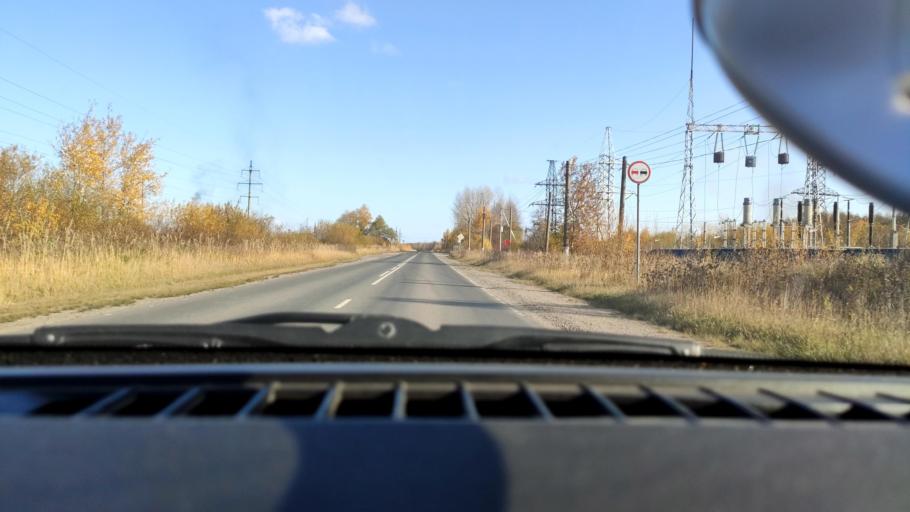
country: RU
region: Perm
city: Gamovo
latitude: 57.8903
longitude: 56.1749
